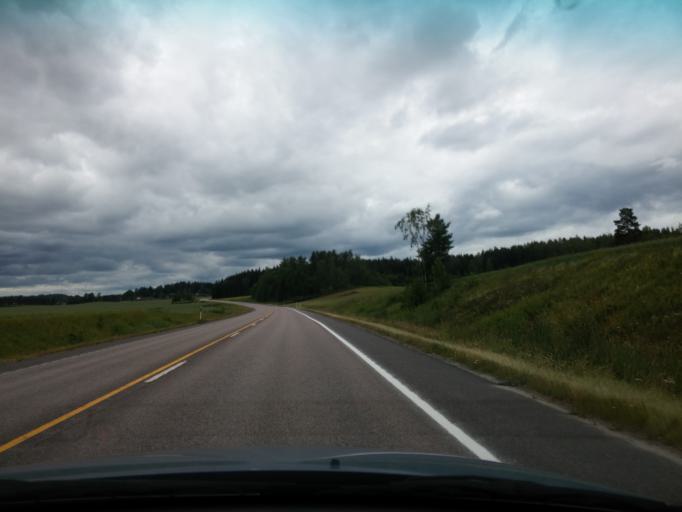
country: FI
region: Uusimaa
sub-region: Porvoo
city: Askola
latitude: 60.4809
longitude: 25.5638
